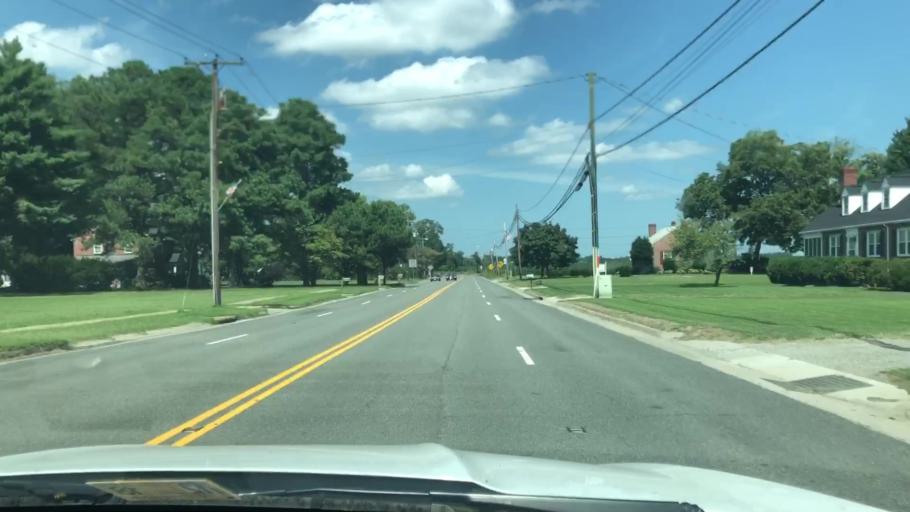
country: US
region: Virginia
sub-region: Richmond County
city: Warsaw
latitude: 37.9528
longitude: -76.7496
